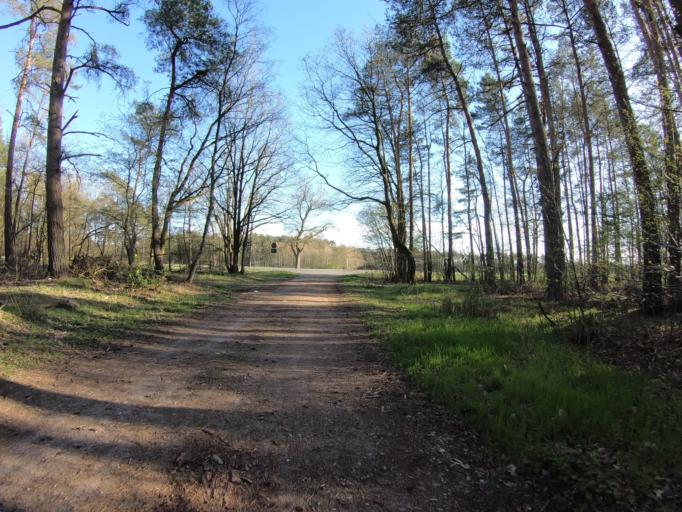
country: DE
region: Lower Saxony
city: Ribbesbuttel
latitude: 52.4846
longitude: 10.4907
